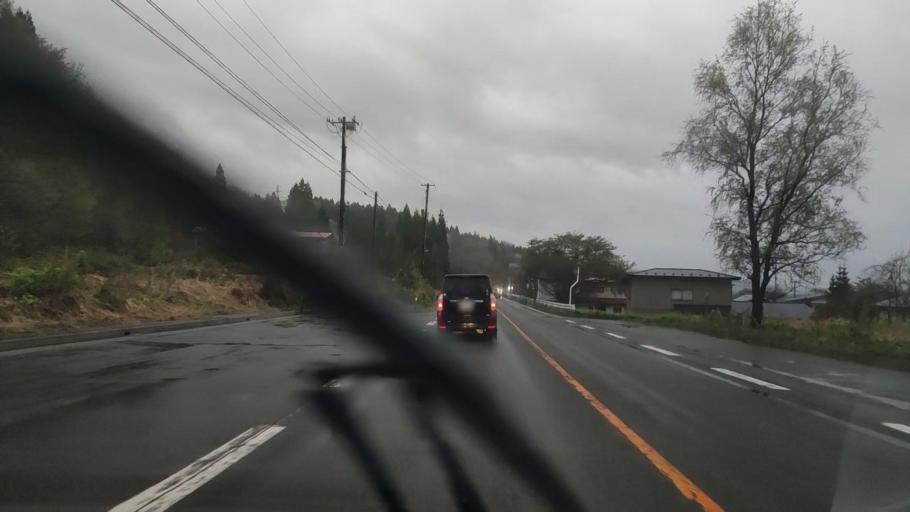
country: JP
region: Akita
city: Akita
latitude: 39.6234
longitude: 140.3201
